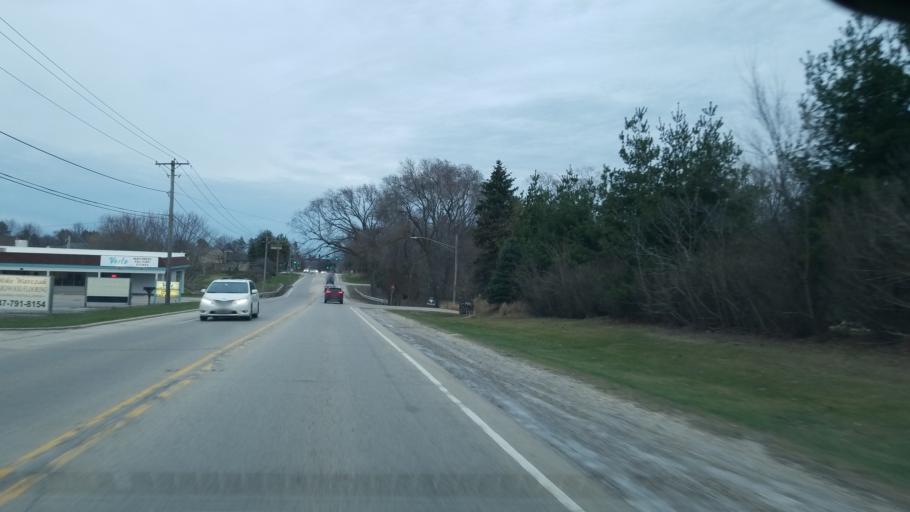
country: US
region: Illinois
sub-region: Kane County
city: Sleepy Hollow
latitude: 42.1007
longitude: -88.3061
